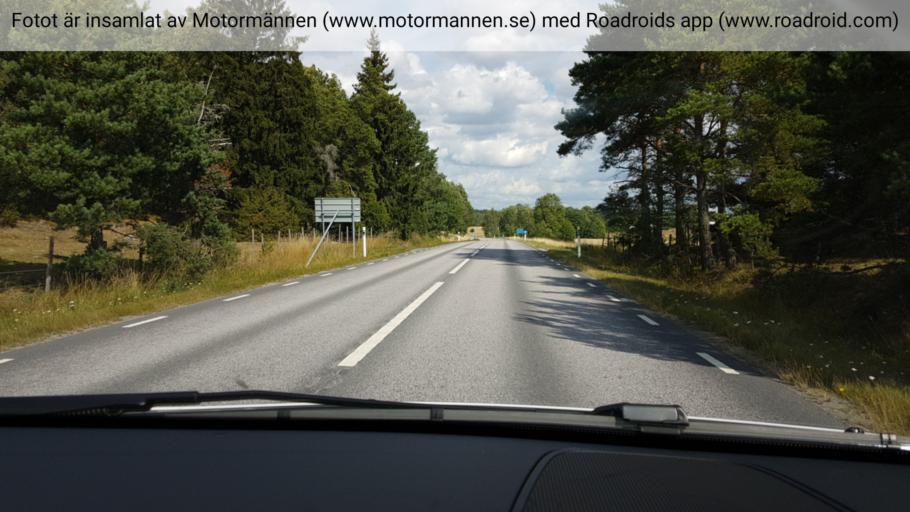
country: SE
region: Stockholm
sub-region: Vallentuna Kommun
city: Vallentuna
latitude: 59.6888
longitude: 18.0434
